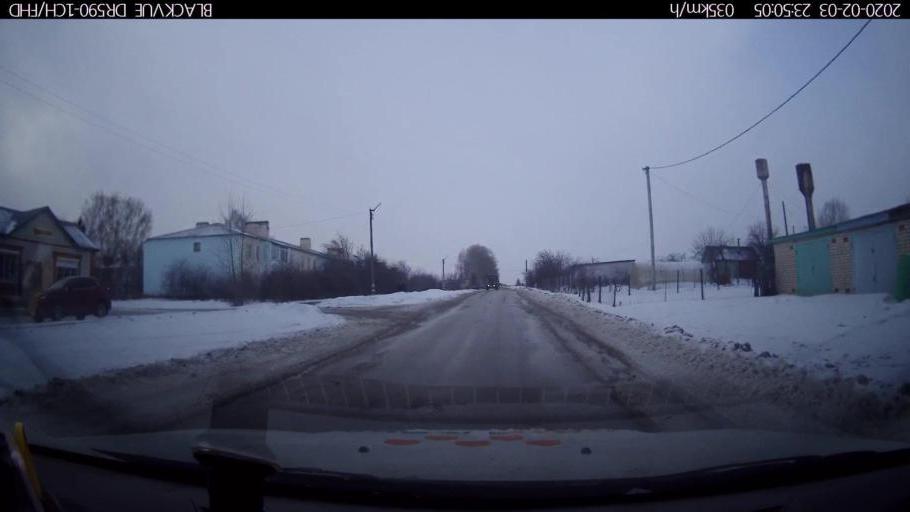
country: RU
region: Nizjnij Novgorod
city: Dal'neye Konstantinovo
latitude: 55.8071
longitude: 44.0813
